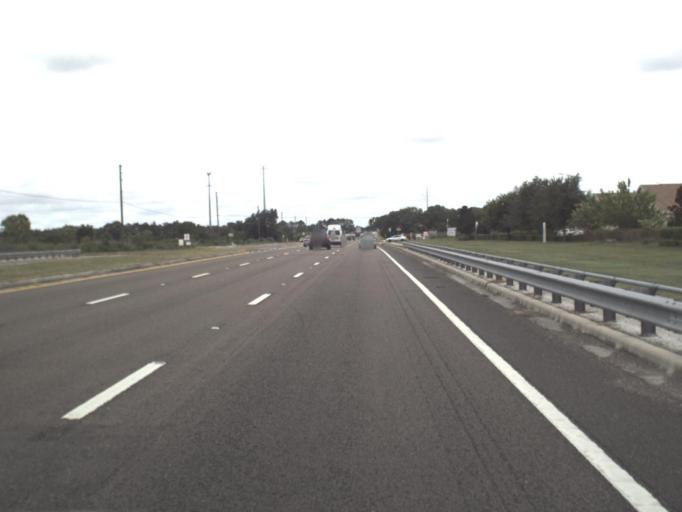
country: US
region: Florida
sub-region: Pasco County
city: Trinity
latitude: 28.2099
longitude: -82.6796
